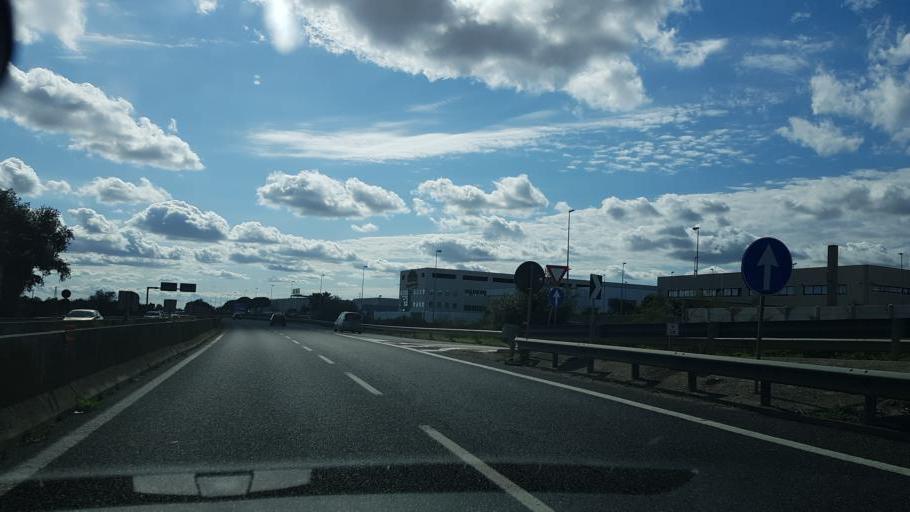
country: IT
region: Apulia
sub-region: Provincia di Lecce
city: Surbo
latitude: 40.4002
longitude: 18.1124
